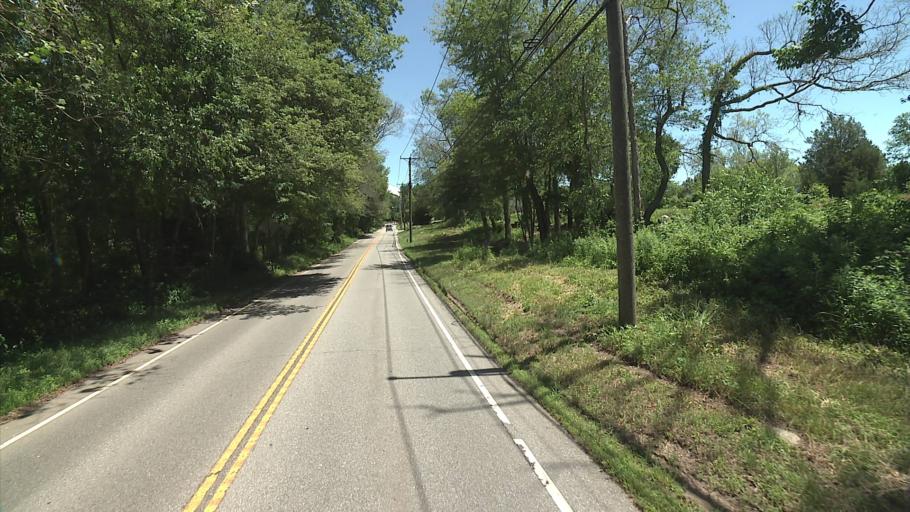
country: US
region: Connecticut
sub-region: New London County
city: Pawcatuck
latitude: 41.3831
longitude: -71.8684
